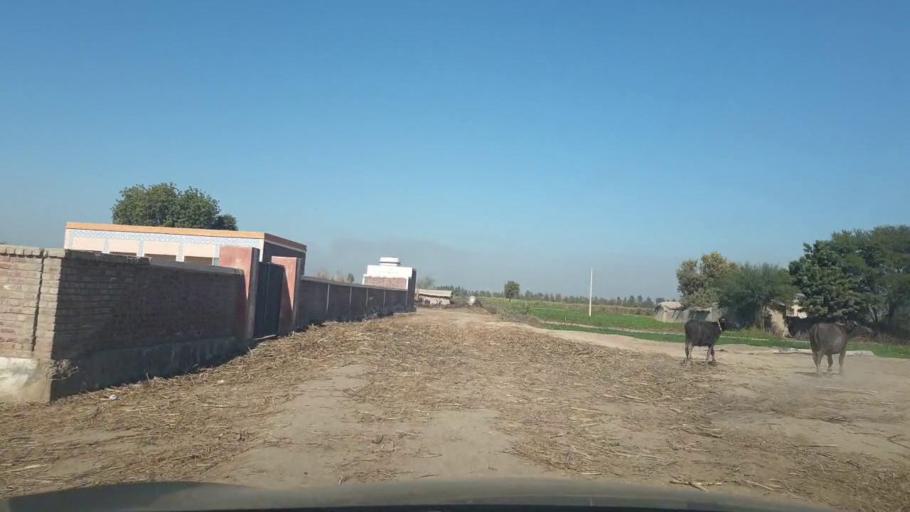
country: PK
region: Sindh
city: Mirpur Mathelo
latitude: 28.0635
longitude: 69.4945
